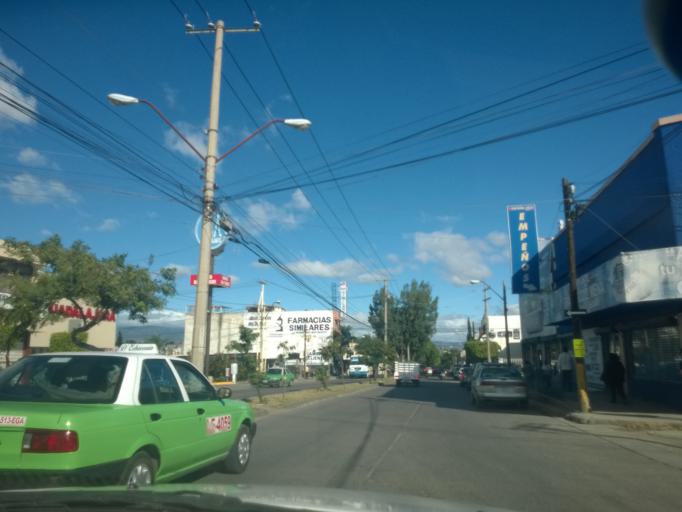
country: MX
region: Guanajuato
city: Leon
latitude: 21.1172
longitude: -101.7068
